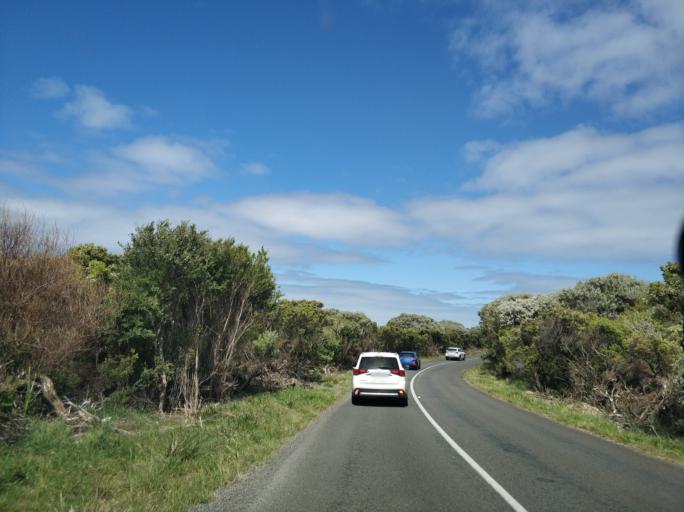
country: AU
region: Victoria
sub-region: Colac-Otway
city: Apollo Bay
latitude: -38.8537
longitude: 143.5194
